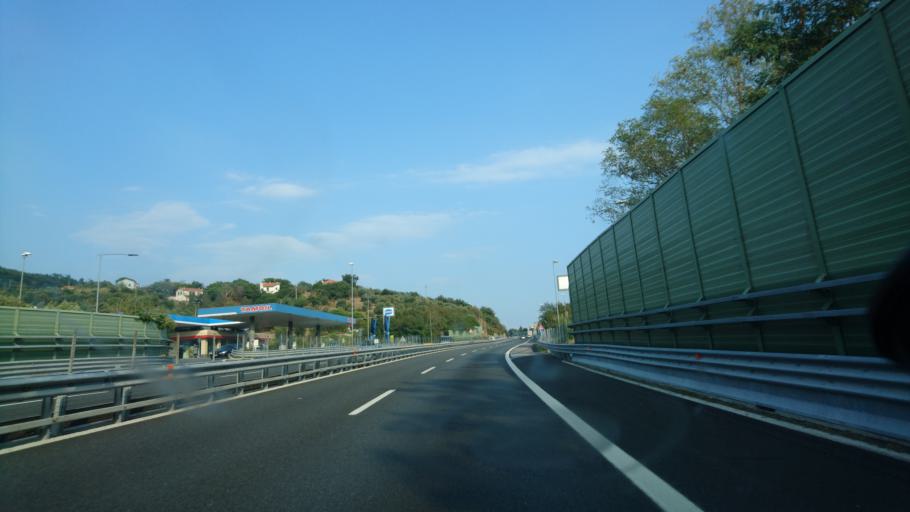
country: IT
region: Liguria
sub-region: Provincia di Savona
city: Savona
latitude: 44.3039
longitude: 8.4520
